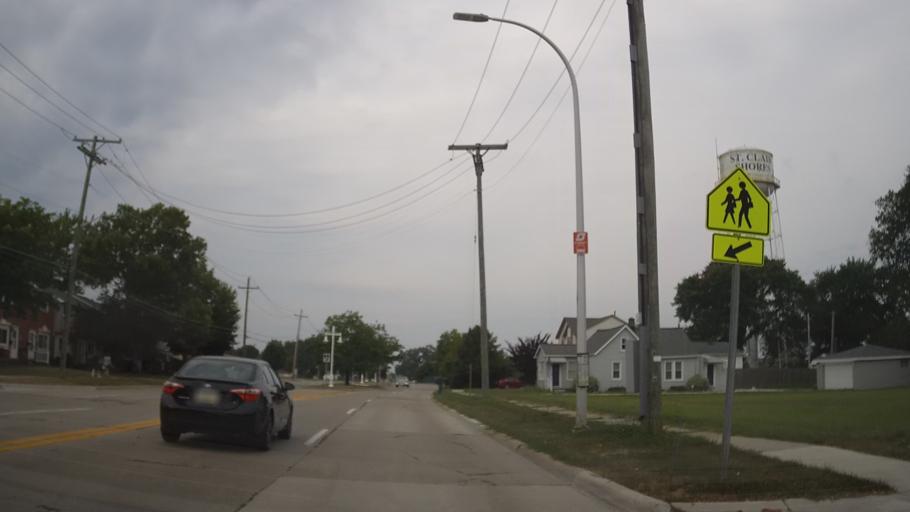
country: US
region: Michigan
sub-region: Macomb County
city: Saint Clair Shores
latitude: 42.5326
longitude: -82.8905
